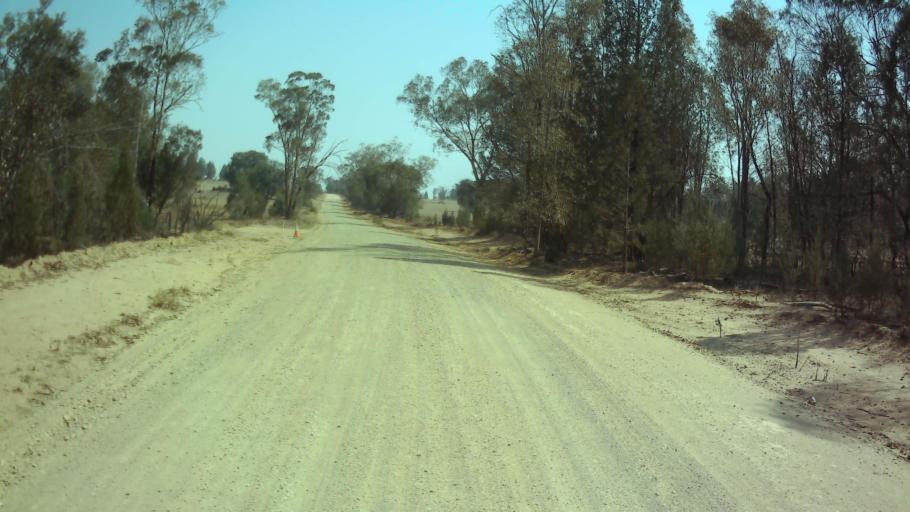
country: AU
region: New South Wales
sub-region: Weddin
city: Grenfell
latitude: -33.6612
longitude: 148.2751
